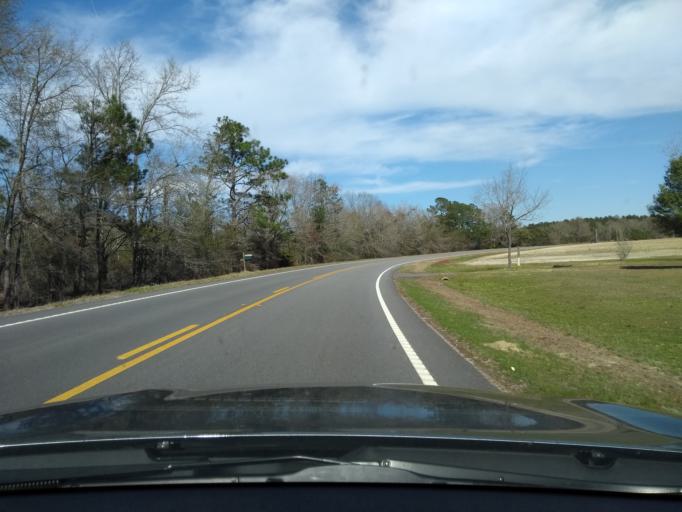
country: US
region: Georgia
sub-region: Bulloch County
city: Brooklet
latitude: 32.4788
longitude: -81.6017
